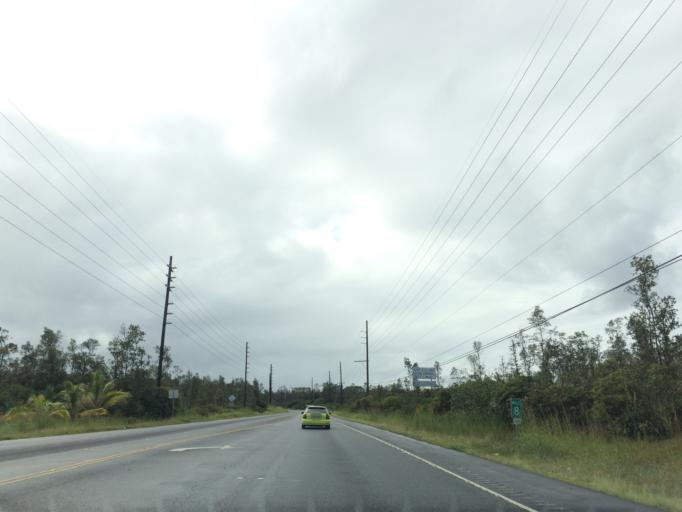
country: US
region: Hawaii
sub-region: Hawaii County
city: Ainaloa
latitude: 19.5300
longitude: -154.9712
